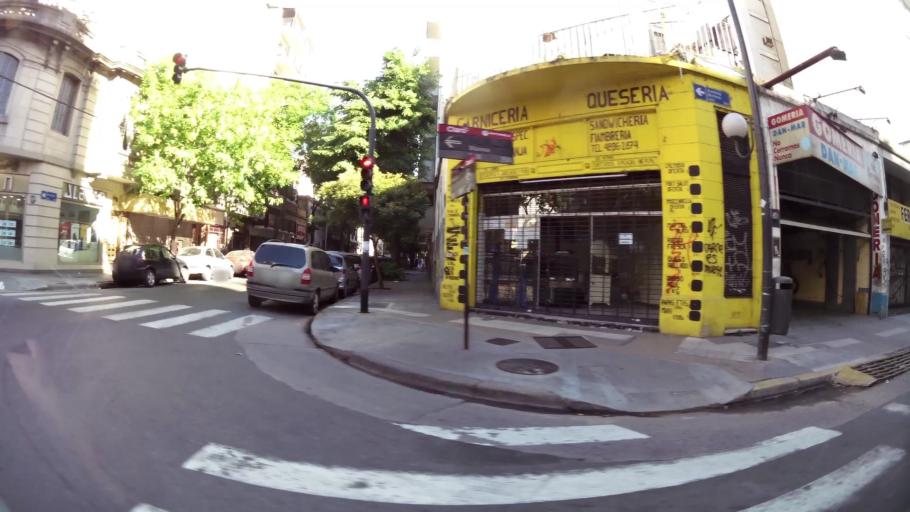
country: AR
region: Buenos Aires F.D.
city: Colegiales
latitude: -34.5595
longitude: -58.4619
